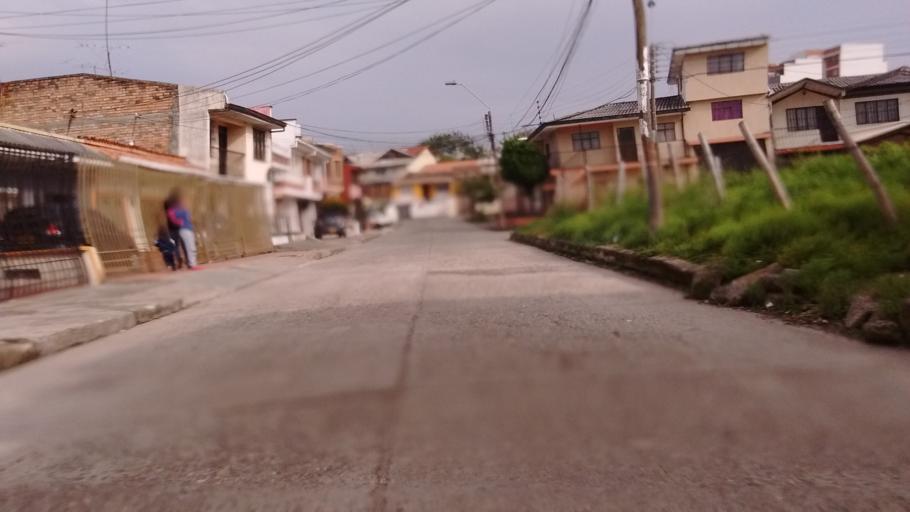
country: CO
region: Cauca
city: Popayan
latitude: 2.4534
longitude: -76.5950
